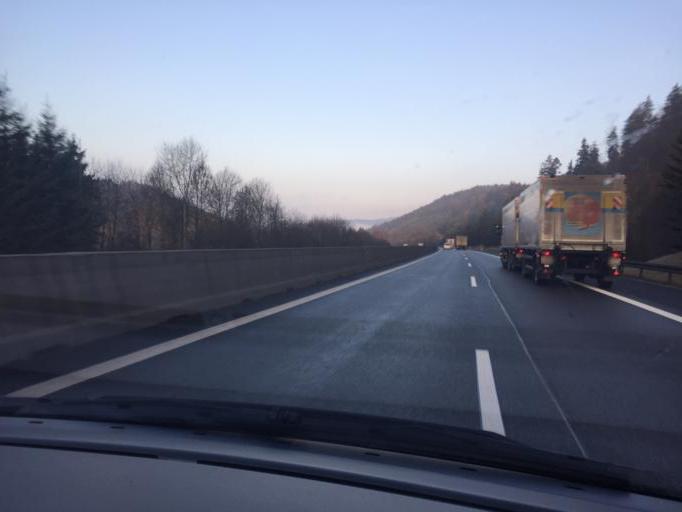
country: DE
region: Baden-Wuerttemberg
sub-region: Freiburg Region
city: Immendingen
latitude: 47.9055
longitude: 8.6970
